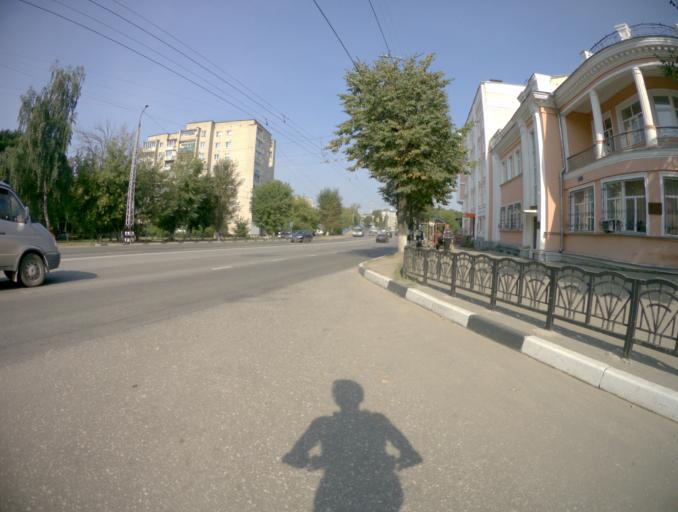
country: RU
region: Vladimir
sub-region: Kovrovskiy Rayon
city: Kovrov
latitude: 56.3682
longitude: 41.3110
